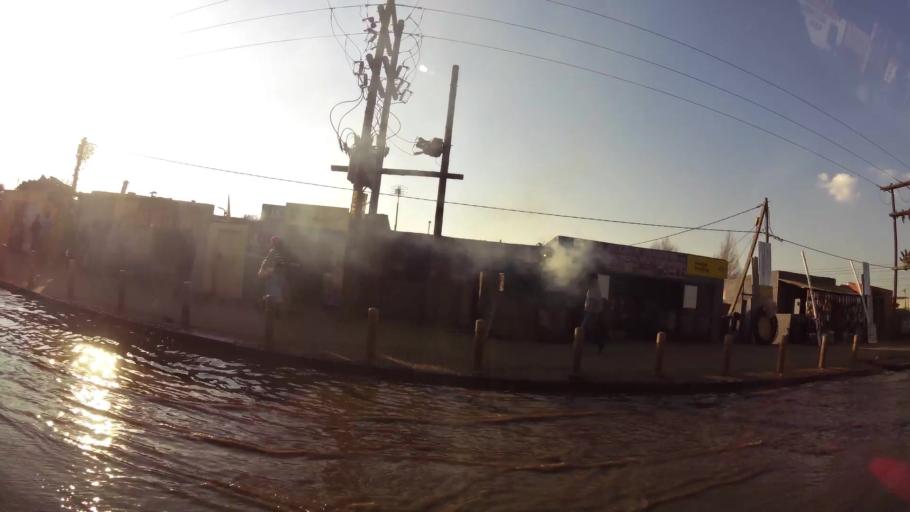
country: ZA
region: Gauteng
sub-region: Ekurhuleni Metropolitan Municipality
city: Tembisa
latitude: -25.9814
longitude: 28.2109
